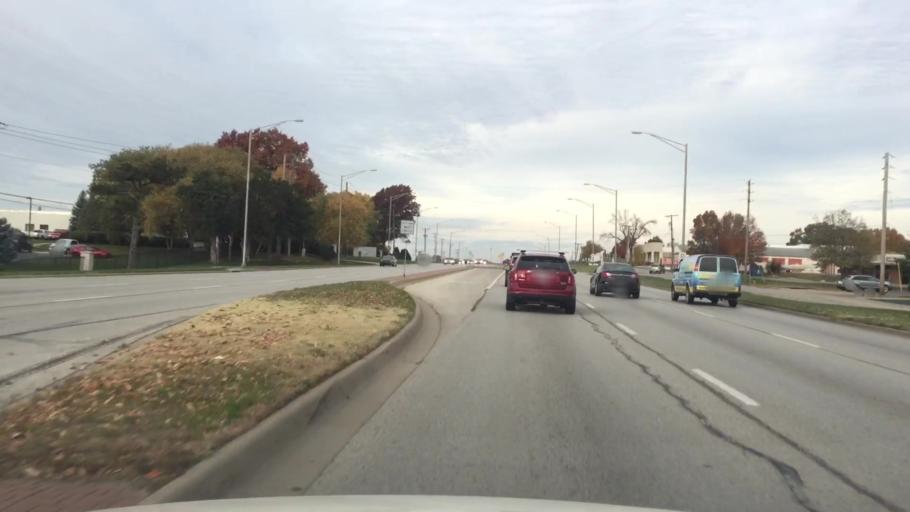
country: US
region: Kansas
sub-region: Johnson County
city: Shawnee
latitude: 39.0148
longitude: -94.7319
